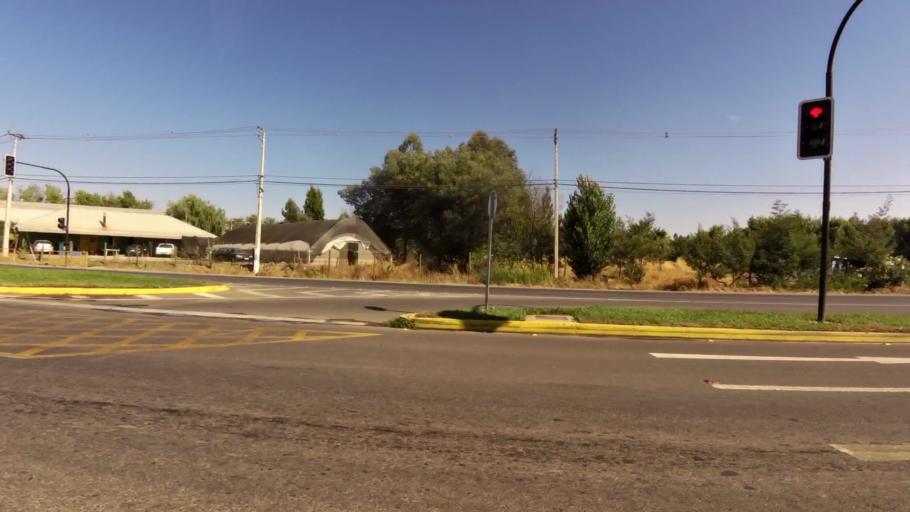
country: CL
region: Maule
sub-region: Provincia de Talca
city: Talca
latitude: -35.3995
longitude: -71.6279
